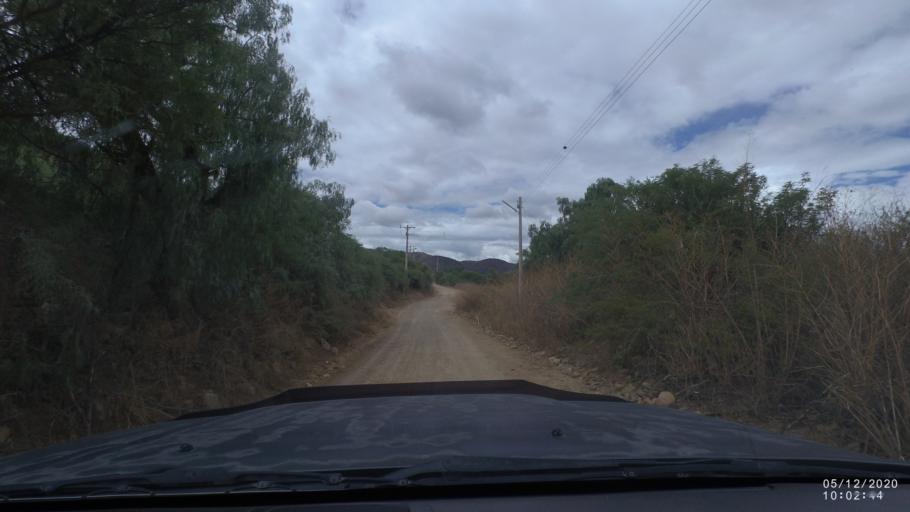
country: BO
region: Cochabamba
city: Sipe Sipe
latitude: -17.4526
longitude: -66.2852
